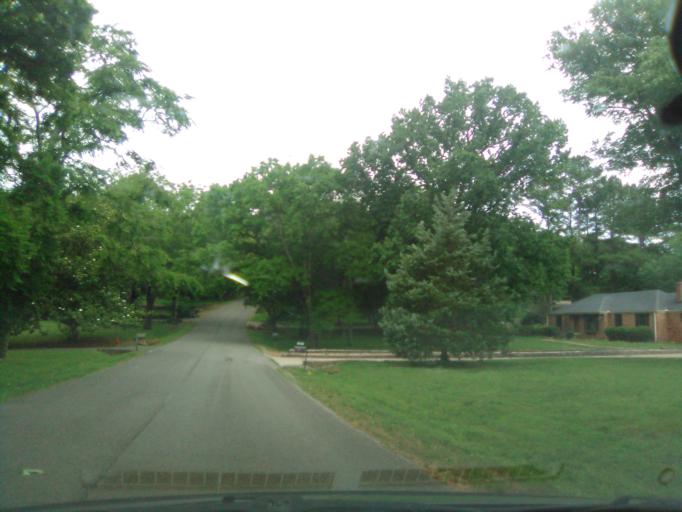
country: US
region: Tennessee
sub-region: Davidson County
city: Belle Meade
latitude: 36.1059
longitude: -86.8905
